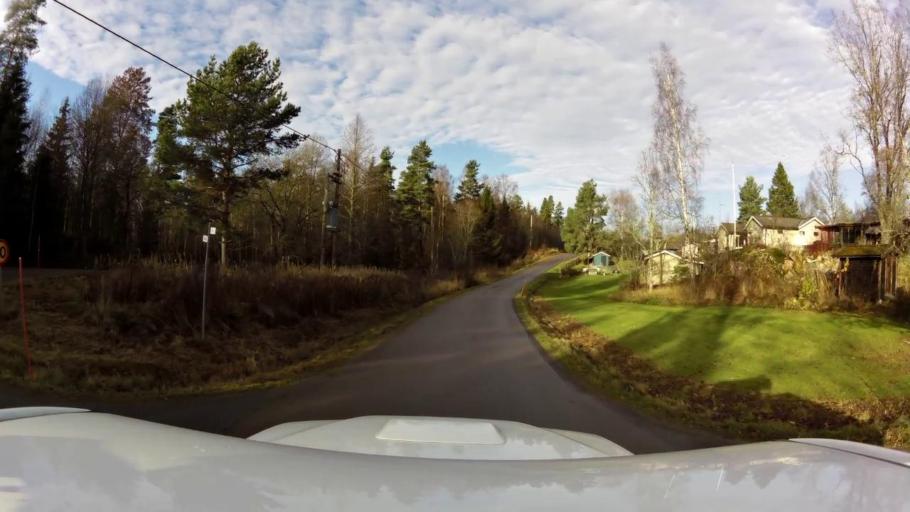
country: SE
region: OEstergoetland
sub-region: Linkopings Kommun
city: Sturefors
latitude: 58.2568
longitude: 15.6964
